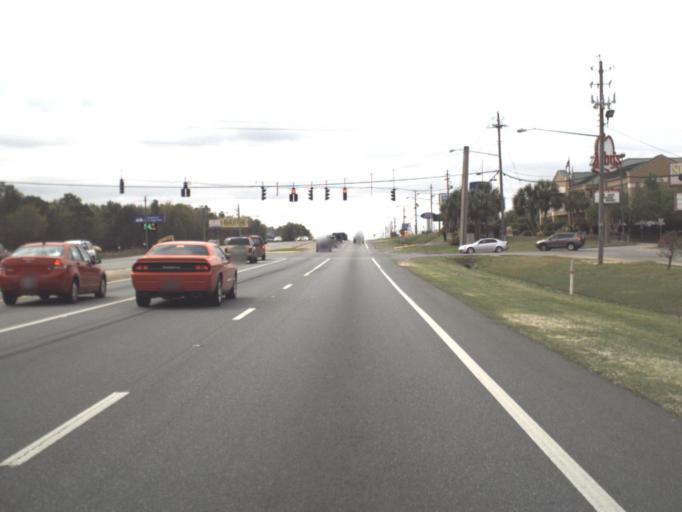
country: US
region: Florida
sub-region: Okaloosa County
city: Crestview
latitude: 30.7215
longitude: -86.5693
